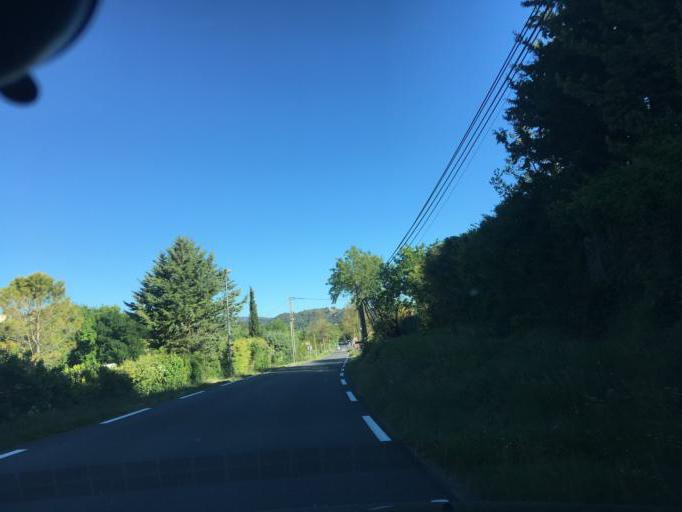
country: FR
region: Provence-Alpes-Cote d'Azur
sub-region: Departement du Var
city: Rians
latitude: 43.6055
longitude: 5.7663
